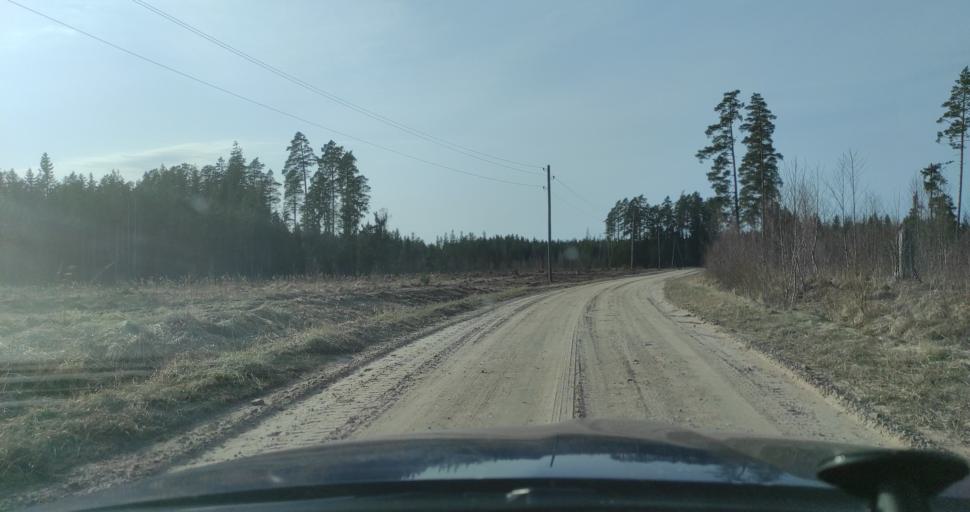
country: LV
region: Kuldigas Rajons
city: Kuldiga
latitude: 57.0130
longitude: 22.0149
